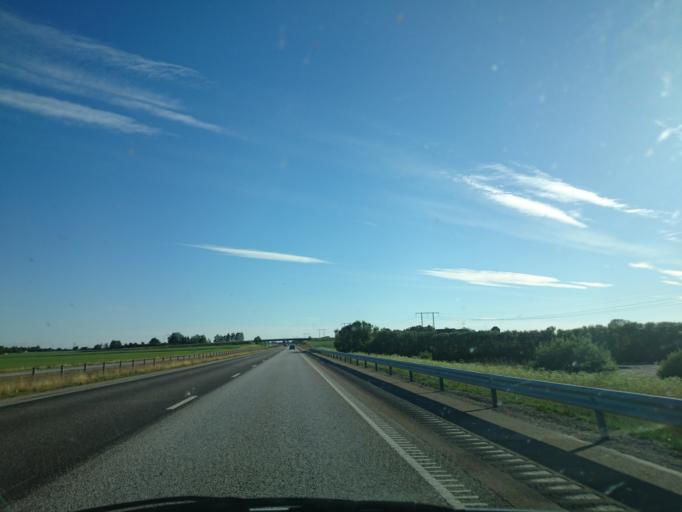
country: SE
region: Skane
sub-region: Astorps Kommun
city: Astorp
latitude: 56.1623
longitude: 12.9670
